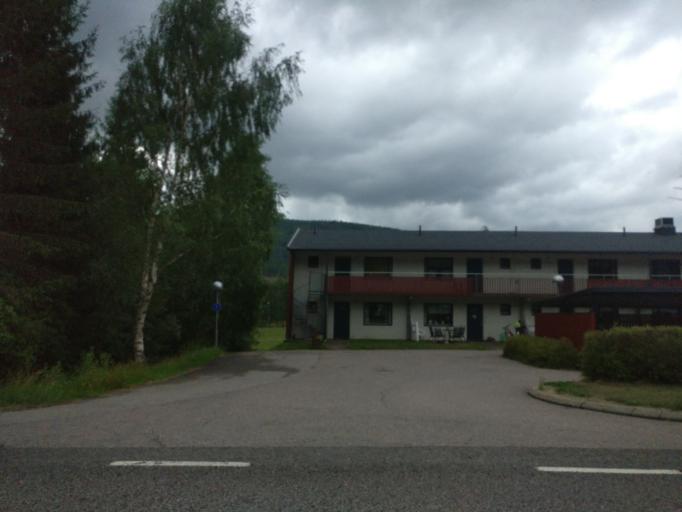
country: SE
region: Vaermland
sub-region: Torsby Kommun
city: Torsby
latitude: 60.7307
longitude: 12.8707
